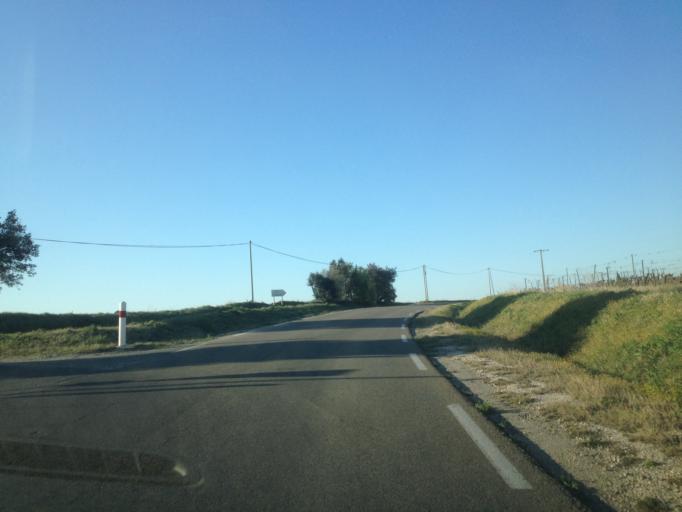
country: FR
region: Provence-Alpes-Cote d'Azur
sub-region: Departement du Vaucluse
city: Chateauneuf-du-Pape
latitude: 44.0716
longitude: 4.8337
